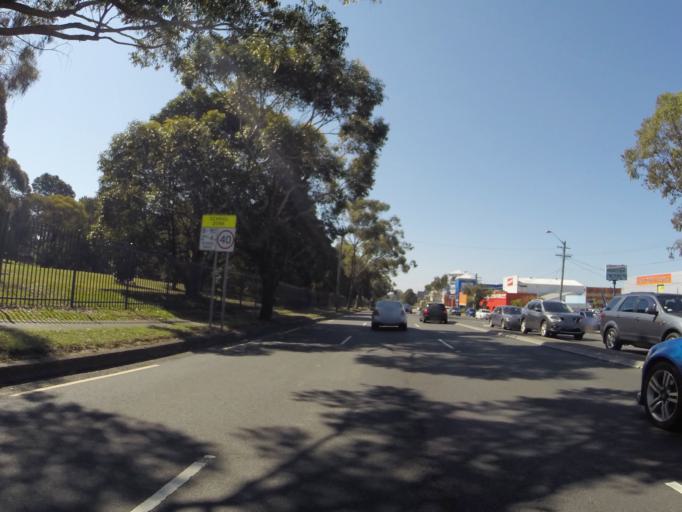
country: AU
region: New South Wales
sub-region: Sutherland Shire
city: Caringbah
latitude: -34.0313
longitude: 151.1195
